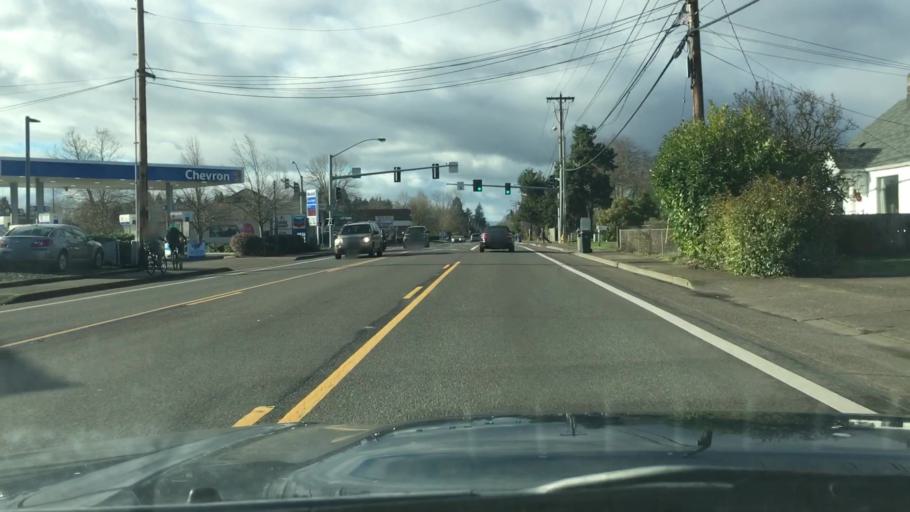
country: US
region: Oregon
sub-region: Lane County
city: Eugene
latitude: 44.0701
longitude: -123.1773
